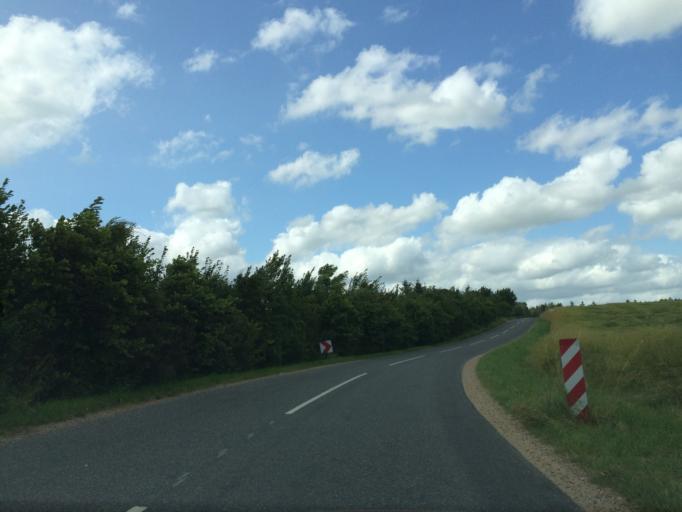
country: DK
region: Central Jutland
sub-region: Skanderborg Kommune
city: Ry
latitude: 56.1894
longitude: 9.7649
